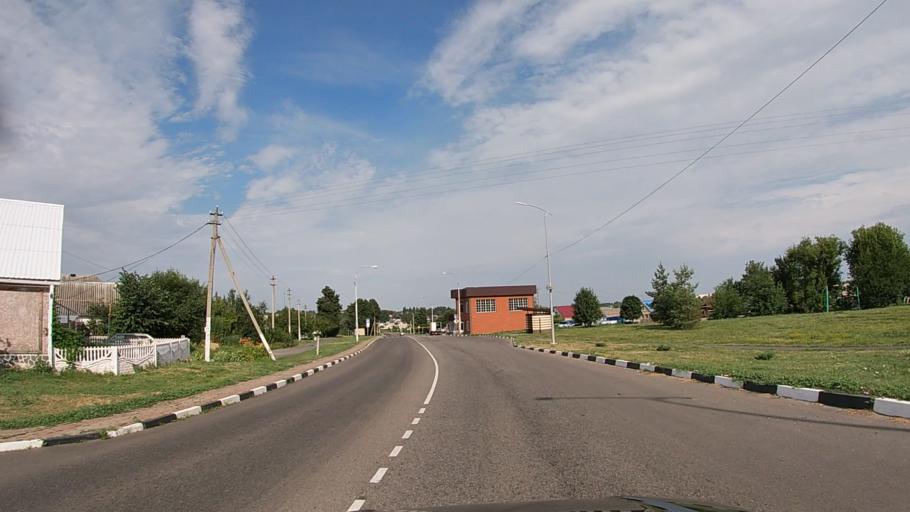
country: RU
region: Belgorod
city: Krasnaya Yaruga
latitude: 50.7996
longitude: 35.6768
